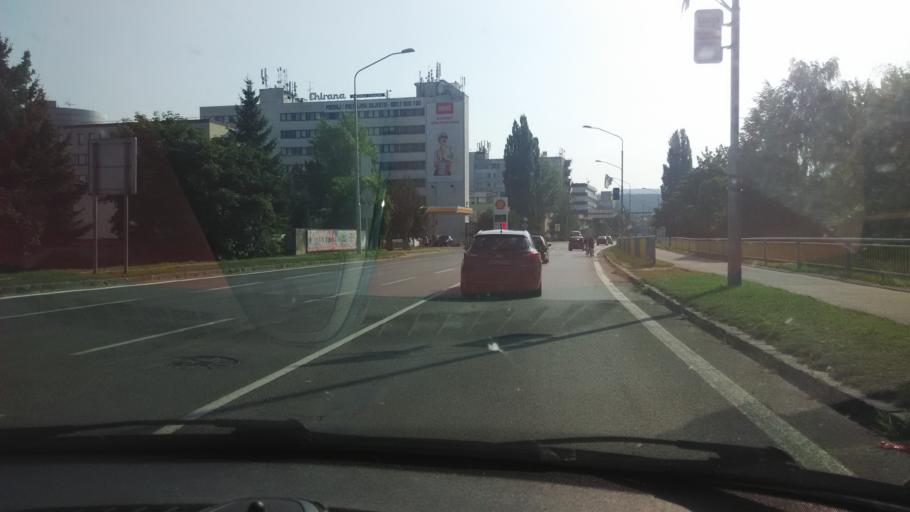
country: SK
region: Trnavsky
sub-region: Okres Trnava
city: Piestany
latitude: 48.5879
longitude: 17.8181
